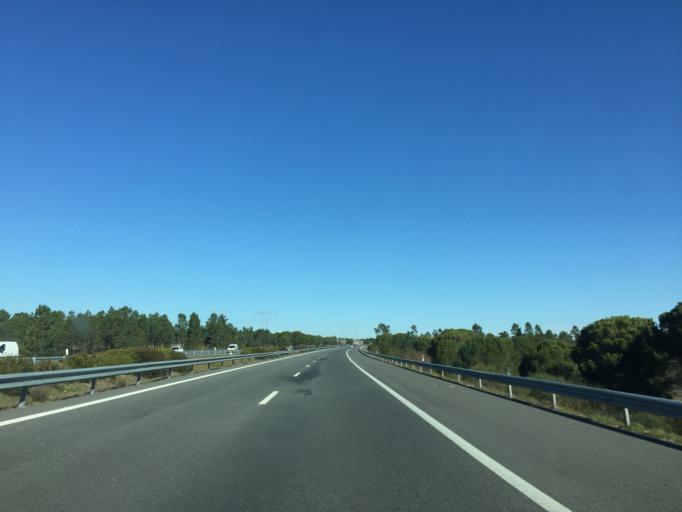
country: PT
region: Setubal
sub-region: Grandola
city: Grandola
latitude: 38.2437
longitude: -8.5235
